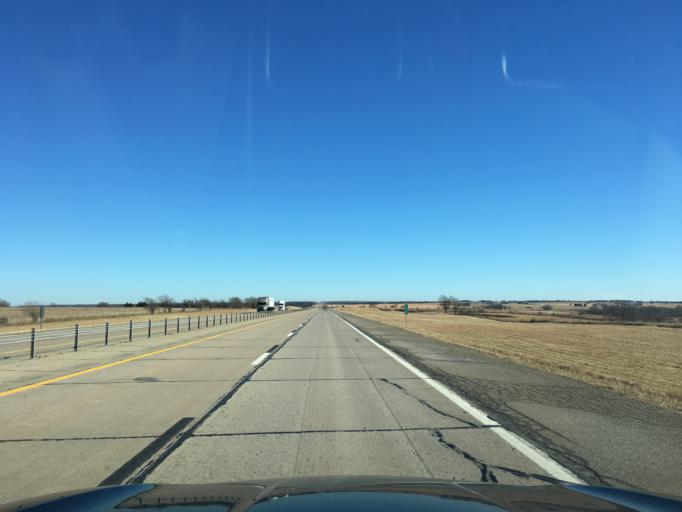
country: US
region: Oklahoma
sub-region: Pawnee County
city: Pawnee
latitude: 36.2254
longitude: -96.8698
